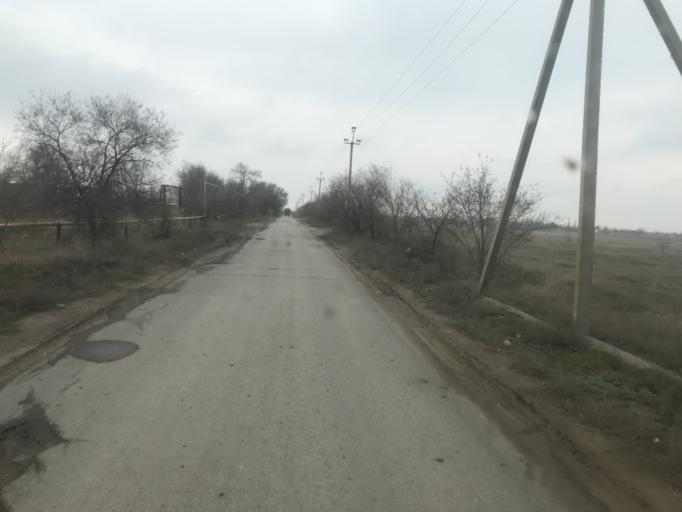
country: RU
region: Volgograd
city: Krasnoslobodsk
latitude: 48.5300
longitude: 44.6091
